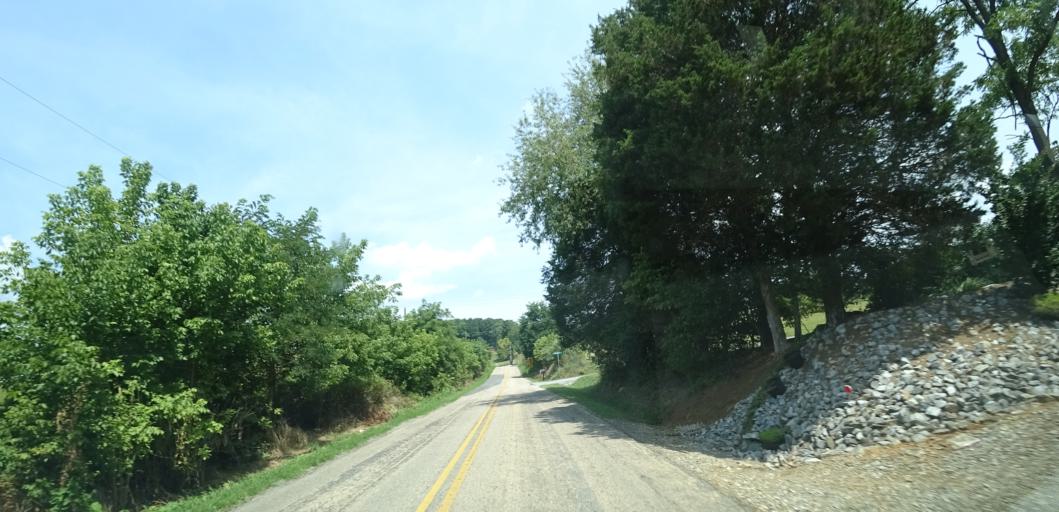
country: US
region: Virginia
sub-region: Botetourt County
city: Fincastle
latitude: 37.4715
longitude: -79.8443
